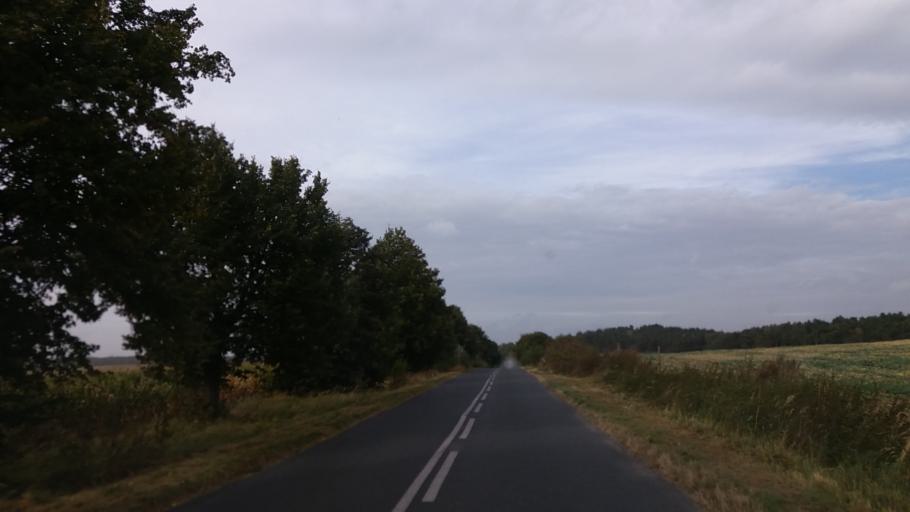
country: PL
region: West Pomeranian Voivodeship
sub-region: Powiat choszczenski
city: Krzecin
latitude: 53.0647
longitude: 15.4926
